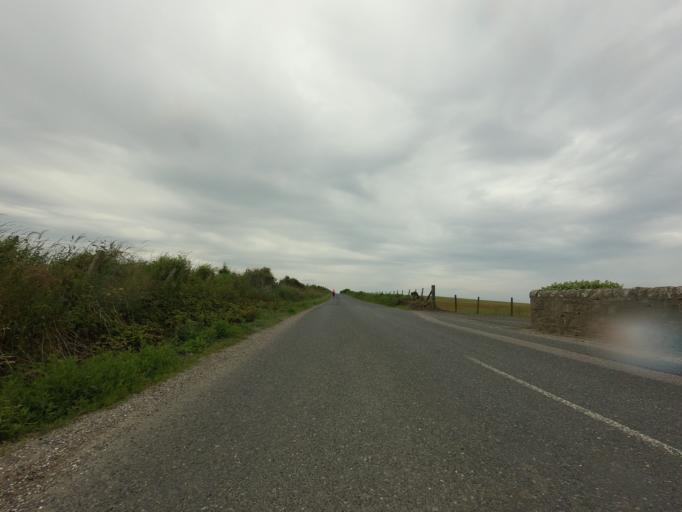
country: GB
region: Scotland
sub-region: Aberdeenshire
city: Whitehills
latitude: 57.6715
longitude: -2.6232
